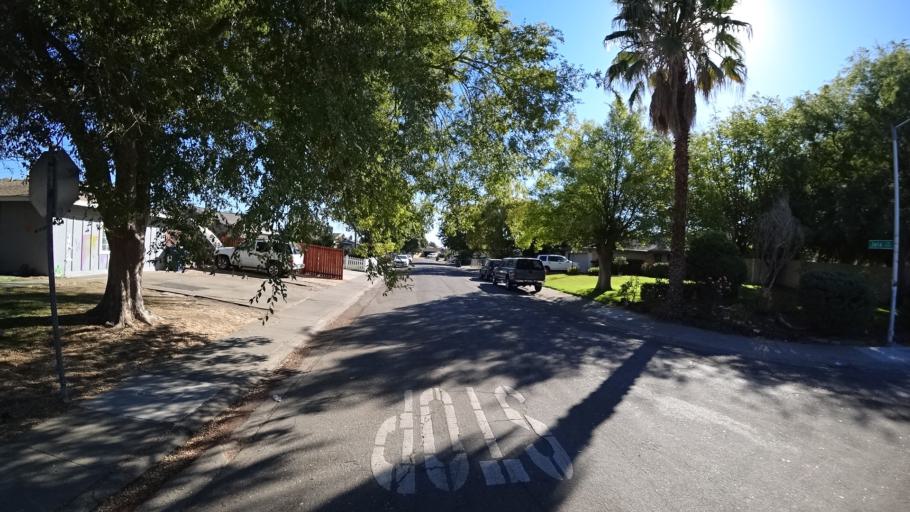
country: US
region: California
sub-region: Sacramento County
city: Parkway
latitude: 38.4804
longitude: -121.4682
